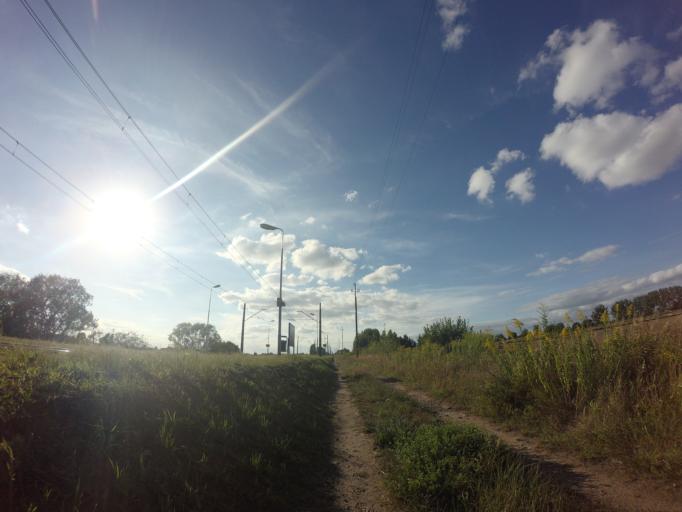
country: PL
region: West Pomeranian Voivodeship
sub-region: Powiat choszczenski
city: Choszczno
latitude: 53.1330
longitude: 15.4533
